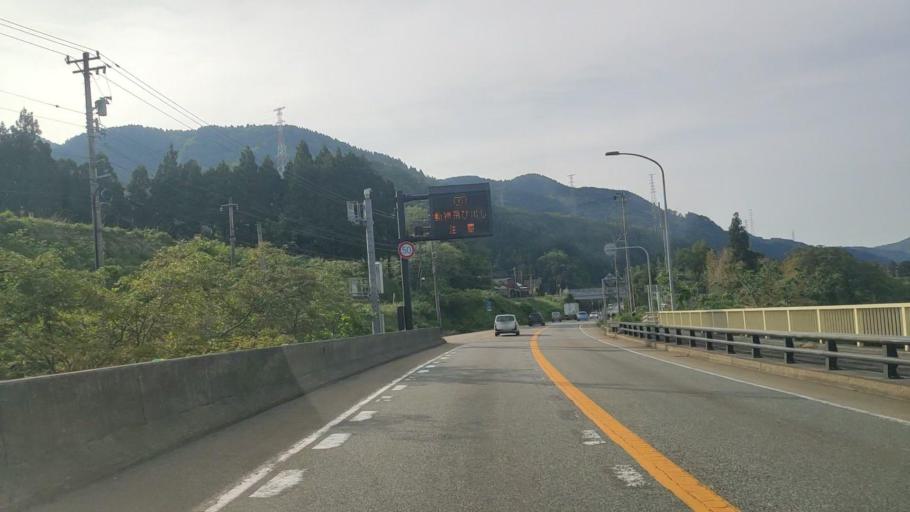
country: JP
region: Toyama
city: Yatsuomachi-higashikumisaka
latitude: 36.5063
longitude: 137.2304
